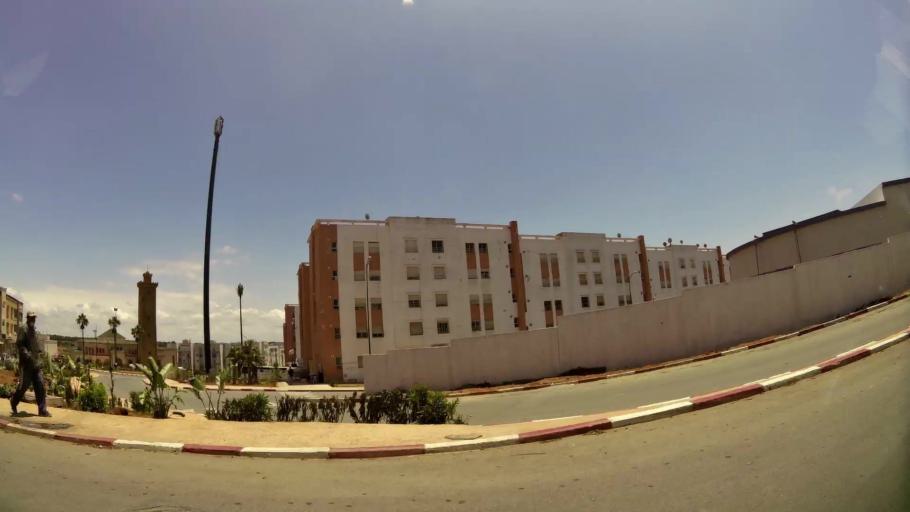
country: MA
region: Gharb-Chrarda-Beni Hssen
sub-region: Kenitra Province
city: Kenitra
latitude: 34.2566
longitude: -6.6503
